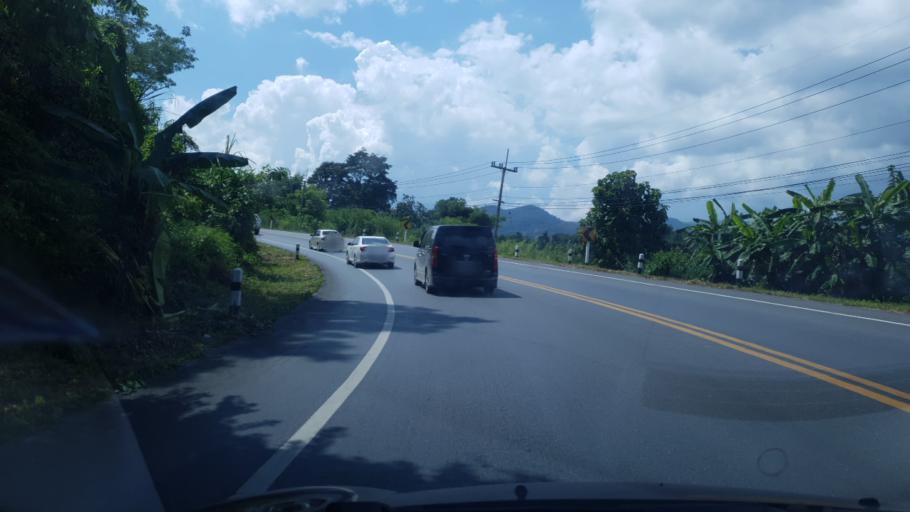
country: TH
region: Chiang Rai
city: Mae Lao
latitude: 19.7366
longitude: 99.6336
